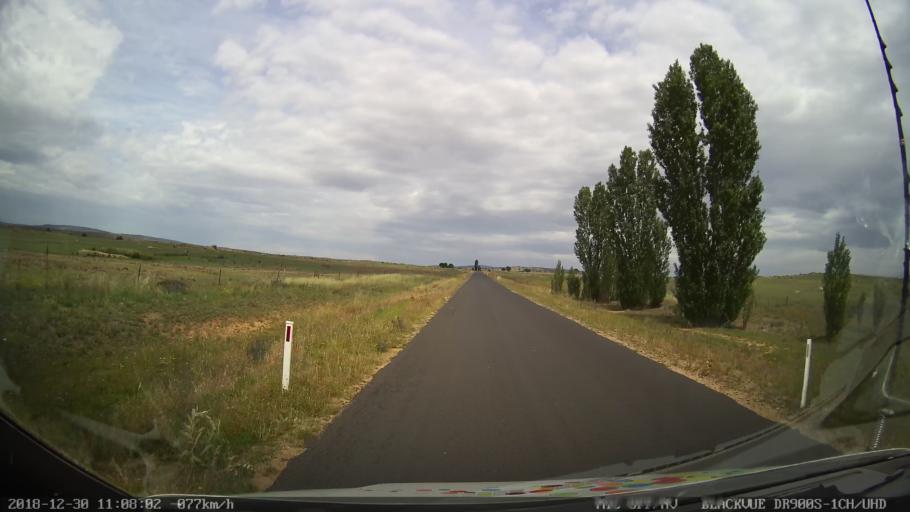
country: AU
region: New South Wales
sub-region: Snowy River
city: Berridale
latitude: -36.5020
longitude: 148.8120
